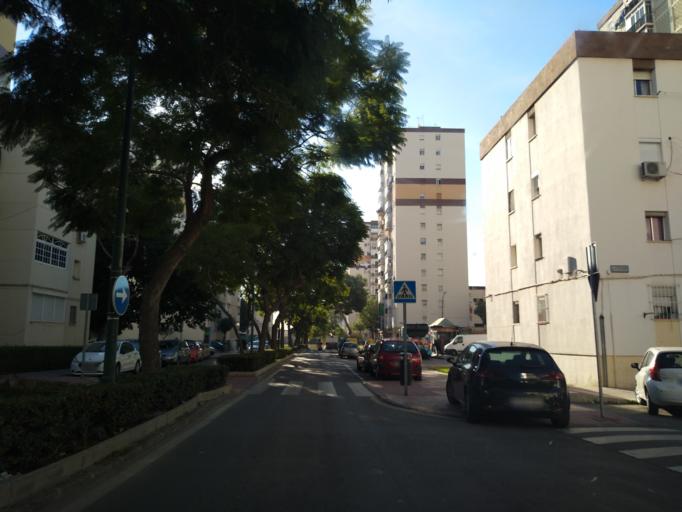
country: ES
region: Andalusia
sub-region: Provincia de Malaga
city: Malaga
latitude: 36.7391
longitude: -4.4324
